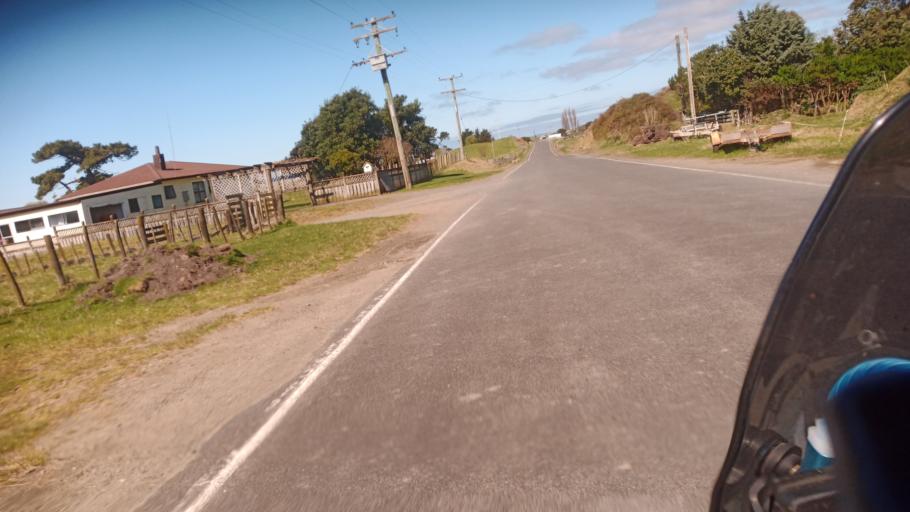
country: NZ
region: Gisborne
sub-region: Gisborne District
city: Gisborne
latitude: -39.0478
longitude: 177.8666
